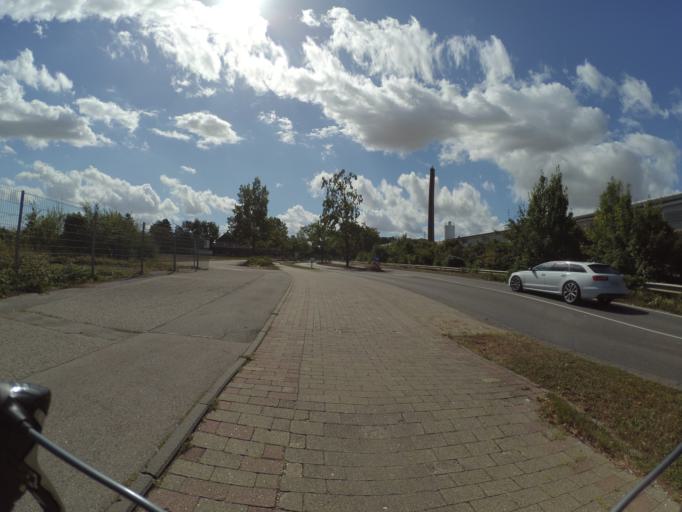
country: DE
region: North Rhine-Westphalia
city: Julich
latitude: 50.9038
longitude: 6.3484
